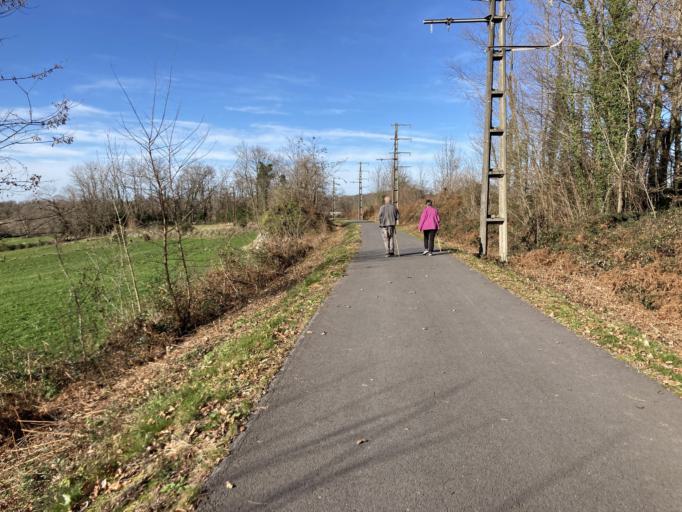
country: FR
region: Aquitaine
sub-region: Departement des Pyrenees-Atlantiques
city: Arudy
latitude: 43.1391
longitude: -0.4481
